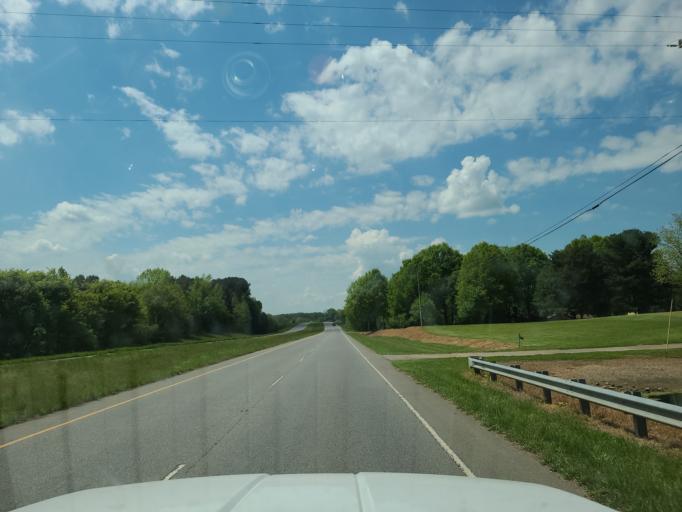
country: US
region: North Carolina
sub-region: Gaston County
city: Cherryville
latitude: 35.4137
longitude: -81.3209
